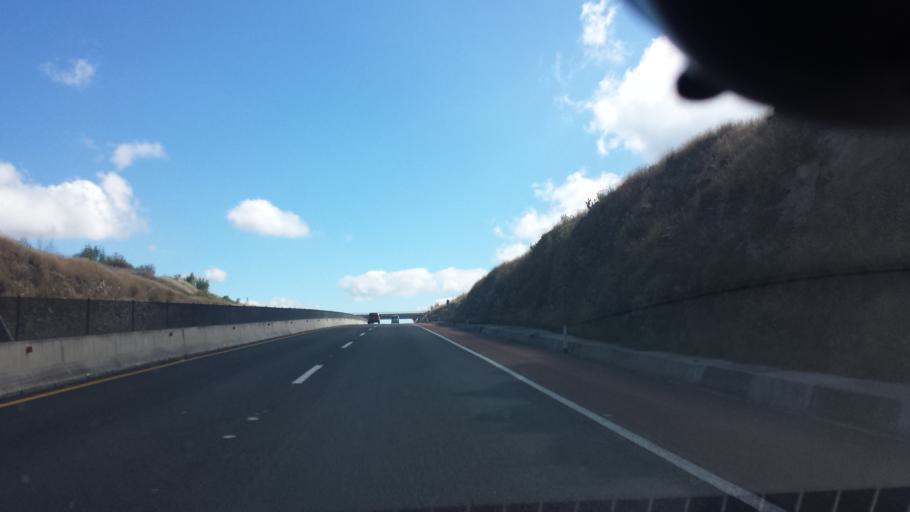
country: MX
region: Mexico
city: San Francisco Soyaniquilpan
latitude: 20.0412
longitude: -99.4478
